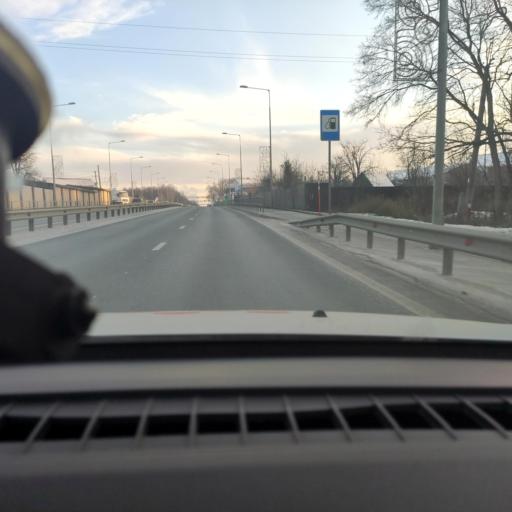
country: RU
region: Samara
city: Petra-Dubrava
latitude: 53.2996
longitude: 50.2429
